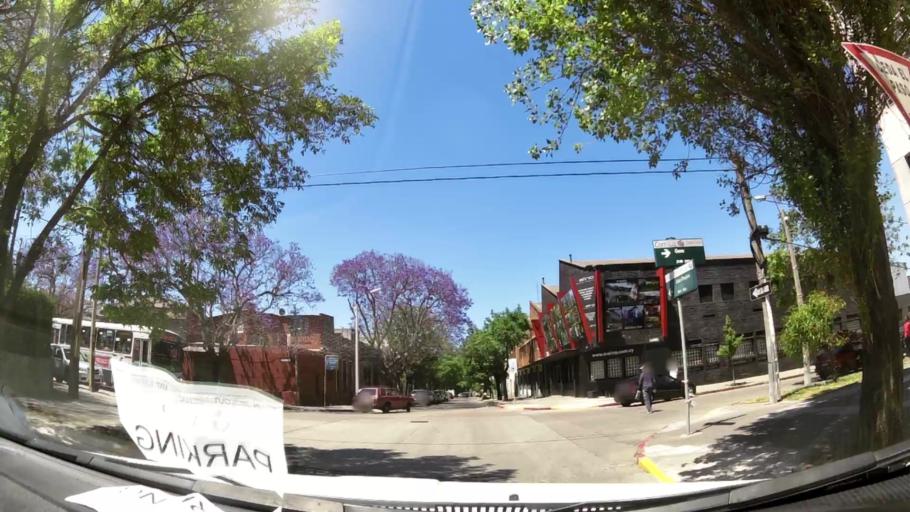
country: UY
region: Montevideo
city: Montevideo
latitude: -34.8931
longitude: -56.1702
